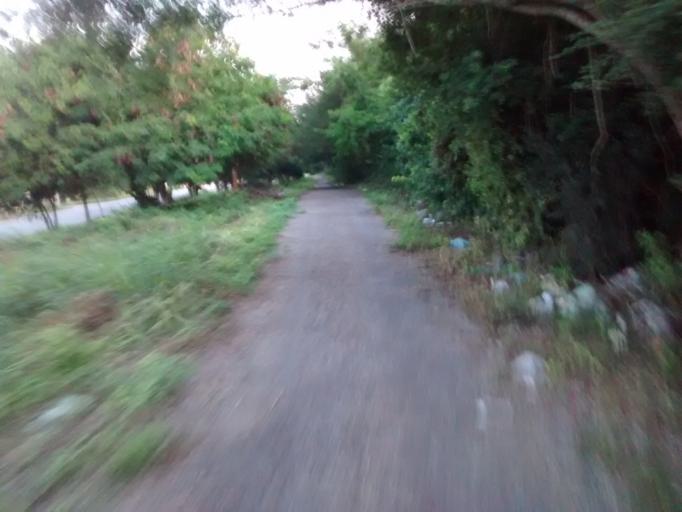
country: MX
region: Yucatan
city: Valladolid
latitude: 20.6930
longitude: -88.2245
